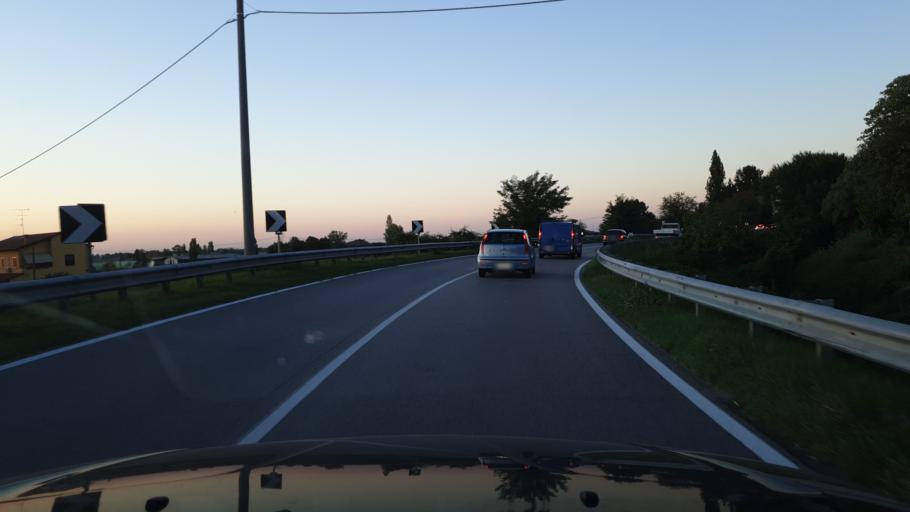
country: IT
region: Emilia-Romagna
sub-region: Provincia di Bologna
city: Ca De Fabbri
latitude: 44.5989
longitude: 11.4383
